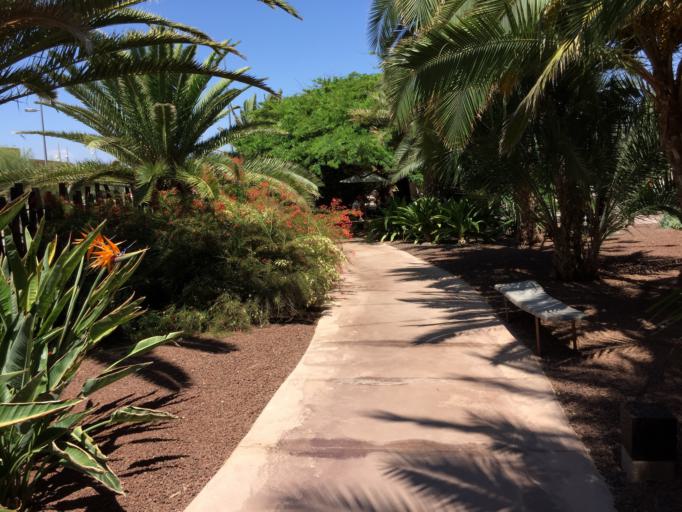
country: ES
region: Canary Islands
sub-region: Provincia de Las Palmas
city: Maspalomas
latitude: 27.7420
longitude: -15.6007
